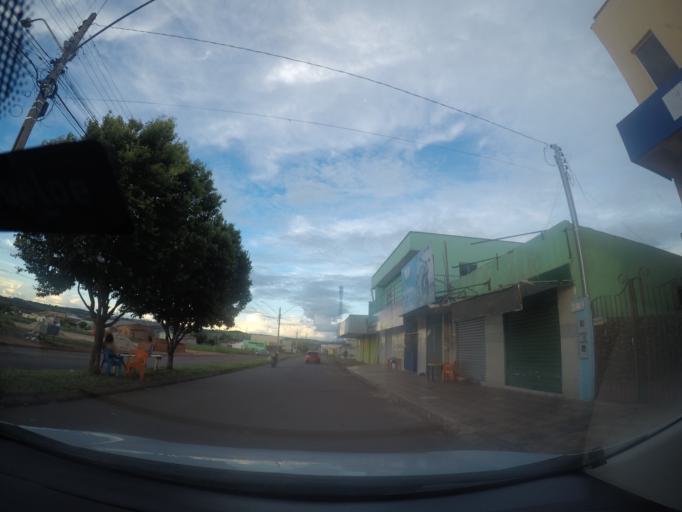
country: BR
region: Goias
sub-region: Goianira
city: Goianira
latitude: -16.5745
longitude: -49.3836
